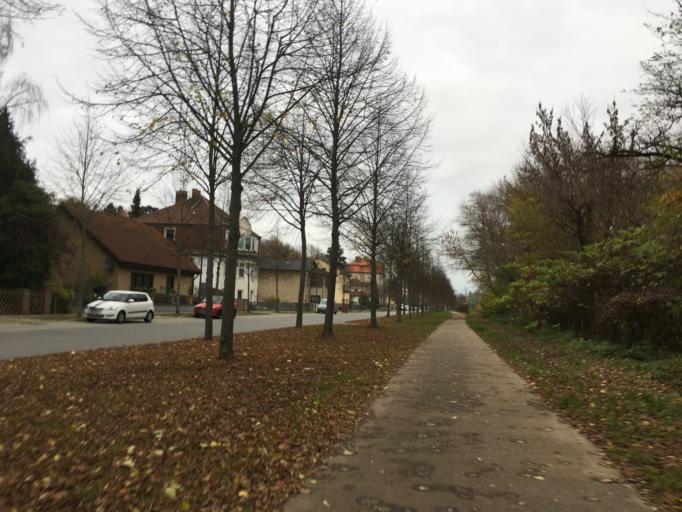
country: DE
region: Brandenburg
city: Frankfurt (Oder)
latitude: 52.3233
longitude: 14.5539
